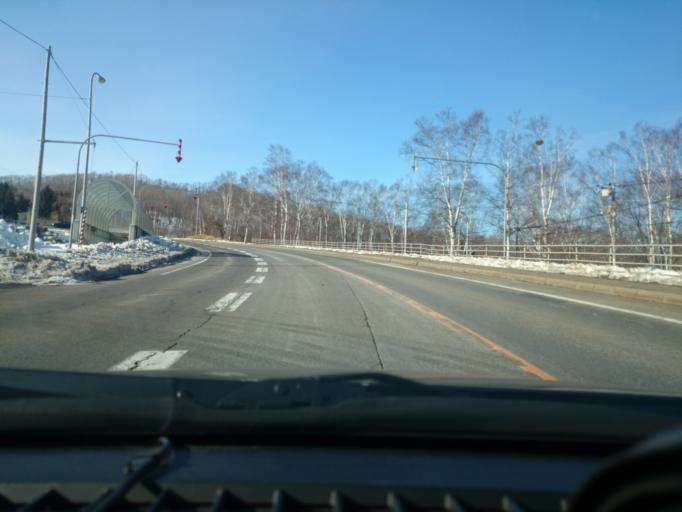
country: JP
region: Hokkaido
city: Otofuke
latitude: 43.2390
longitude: 143.5367
